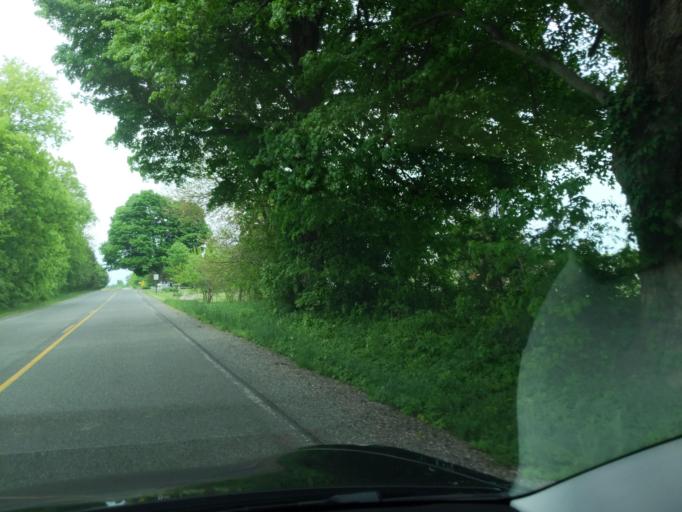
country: US
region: Michigan
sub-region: Ingham County
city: Leslie
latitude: 42.4769
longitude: -84.4236
